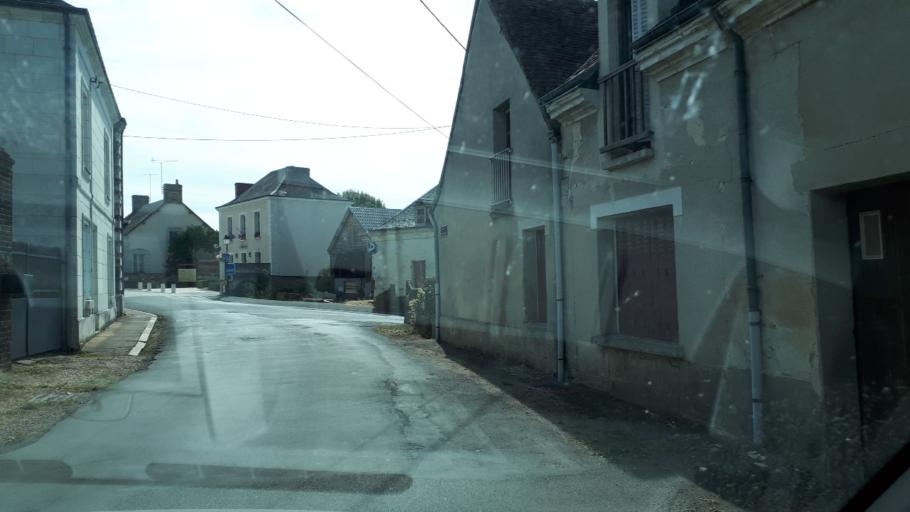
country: FR
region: Centre
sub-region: Departement du Loir-et-Cher
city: Montoire-sur-le-Loir
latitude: 47.7242
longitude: 0.8263
